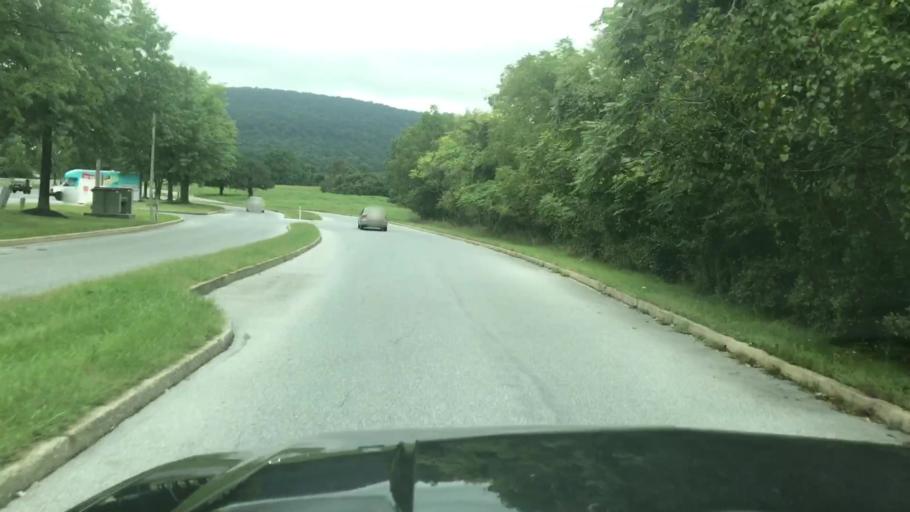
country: US
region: Pennsylvania
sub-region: Dauphin County
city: Lawrence Park
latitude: 40.3326
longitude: -76.8487
